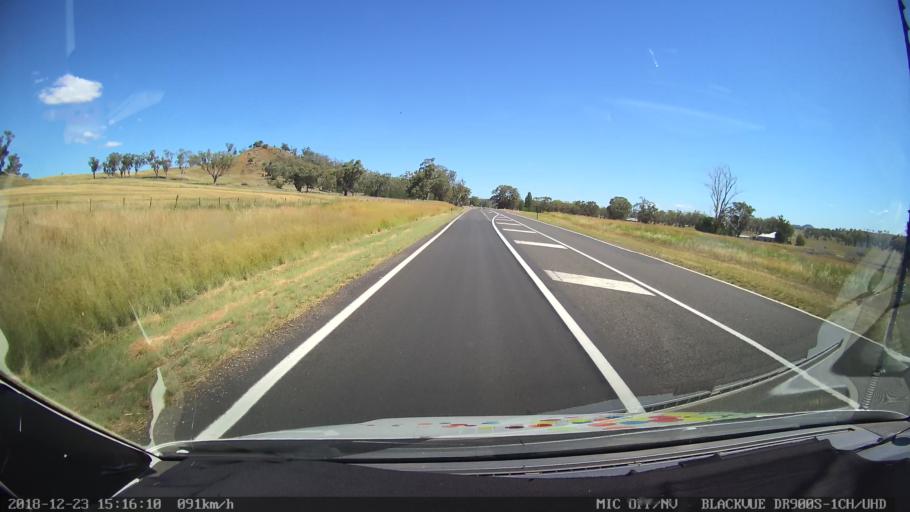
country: AU
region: New South Wales
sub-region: Tamworth Municipality
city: Manilla
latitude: -30.7954
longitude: 150.7471
